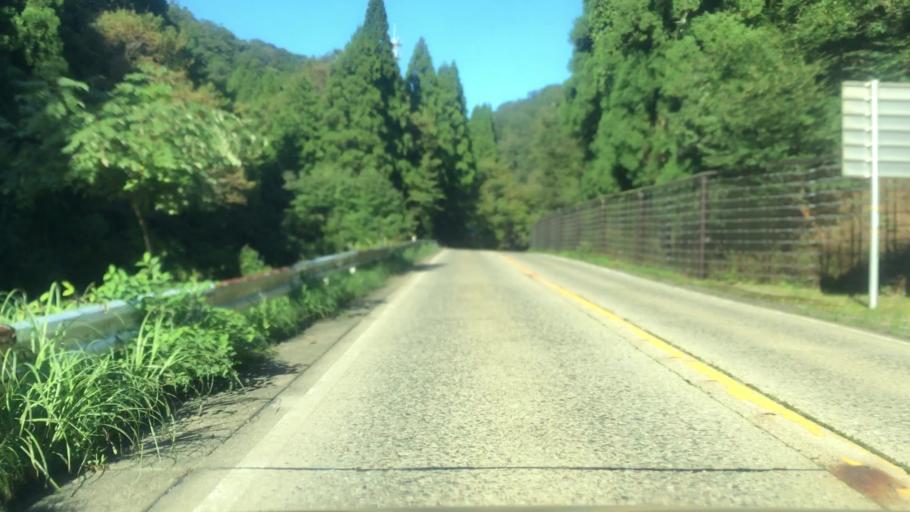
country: JP
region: Hyogo
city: Toyooka
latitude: 35.5818
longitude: 134.8584
